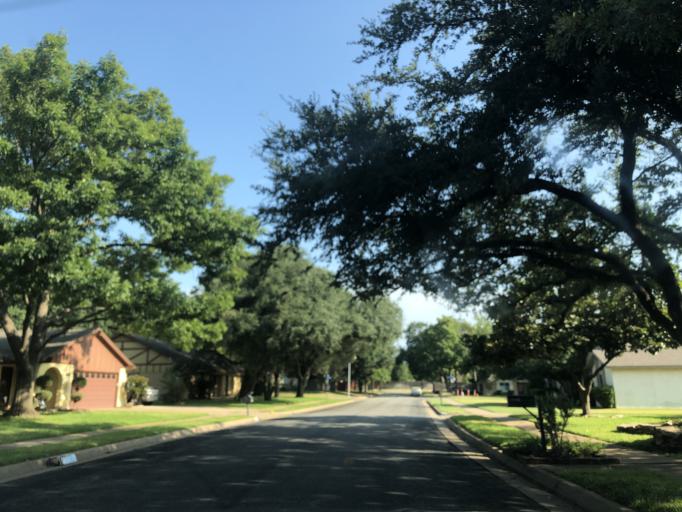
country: US
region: Texas
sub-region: Tarrant County
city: Euless
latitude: 32.8725
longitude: -97.0873
